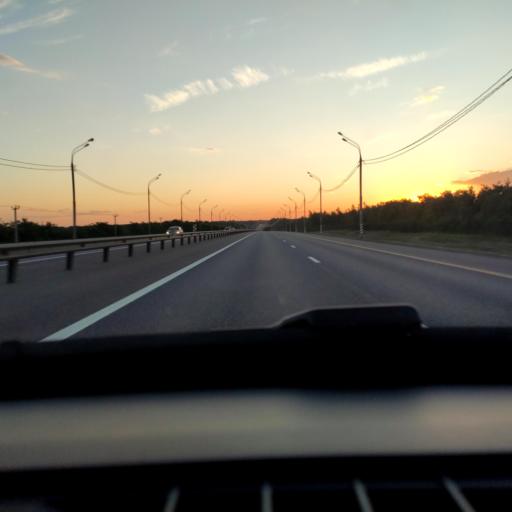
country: RU
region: Lipetsk
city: Zadonsk
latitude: 52.3326
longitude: 39.0007
